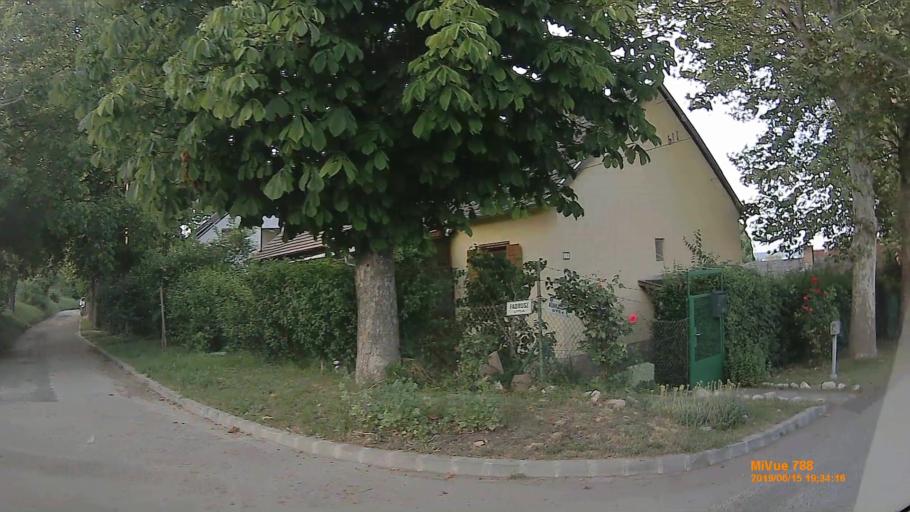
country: HU
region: Veszprem
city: Balatonalmadi
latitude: 47.0189
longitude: 18.0018
